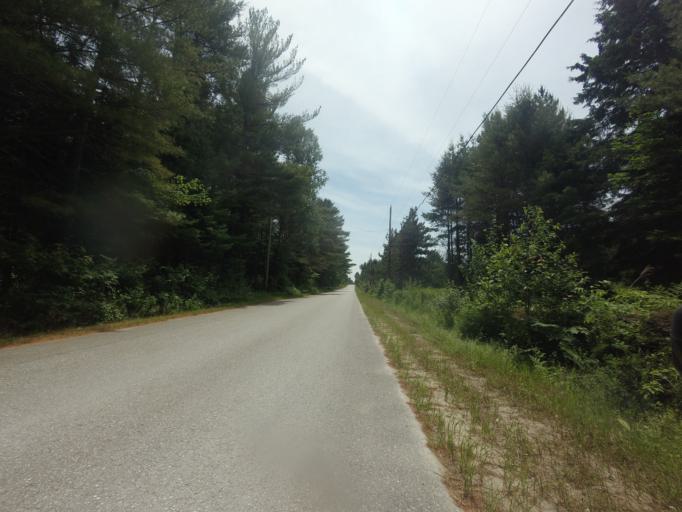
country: CA
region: Quebec
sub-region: Outaouais
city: Wakefield
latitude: 45.9576
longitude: -76.0605
